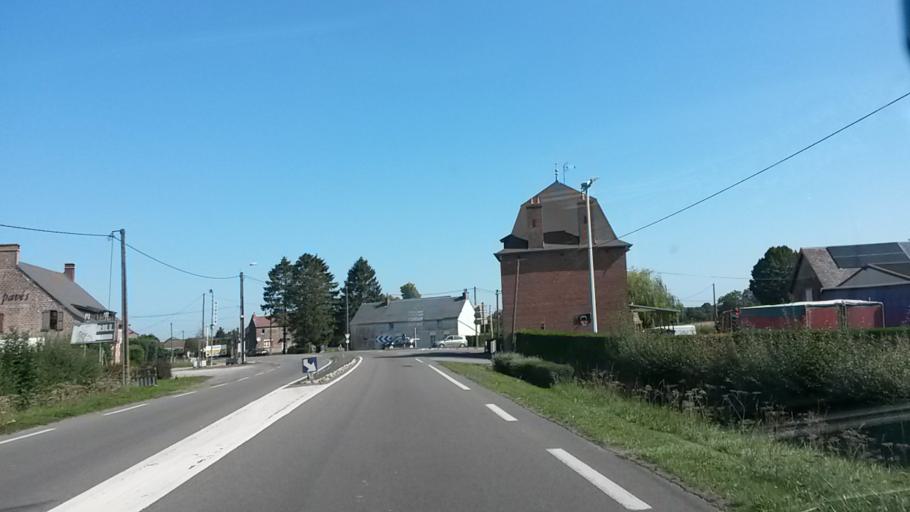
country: FR
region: Nord-Pas-de-Calais
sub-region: Departement du Nord
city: Avesnelles
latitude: 50.1539
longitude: 3.9544
